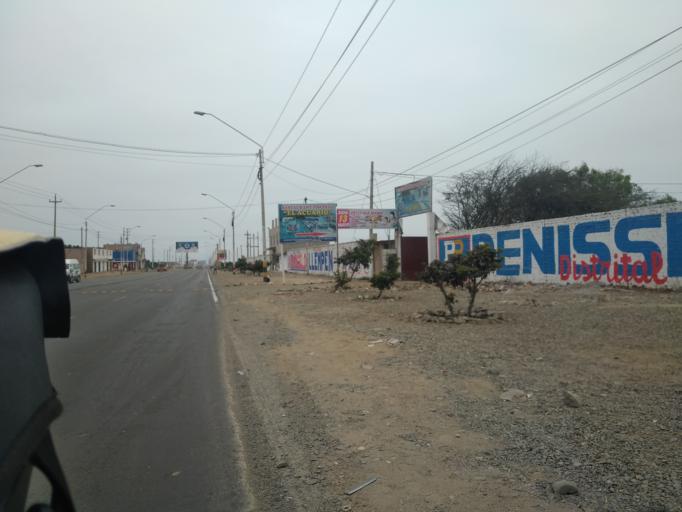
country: PE
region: La Libertad
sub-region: Provincia de Trujillo
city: Huanchaco
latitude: -8.0895
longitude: -79.1031
